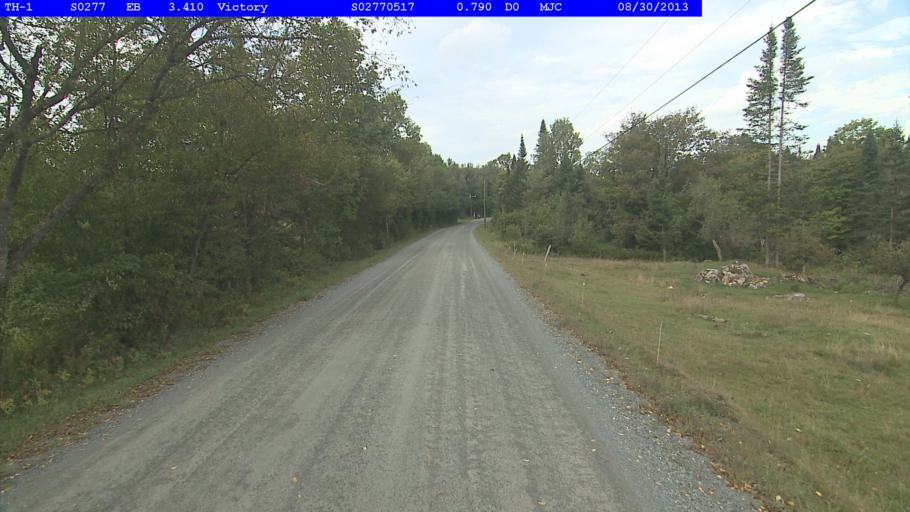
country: US
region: Vermont
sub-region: Caledonia County
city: Lyndonville
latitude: 44.5067
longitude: -71.8482
